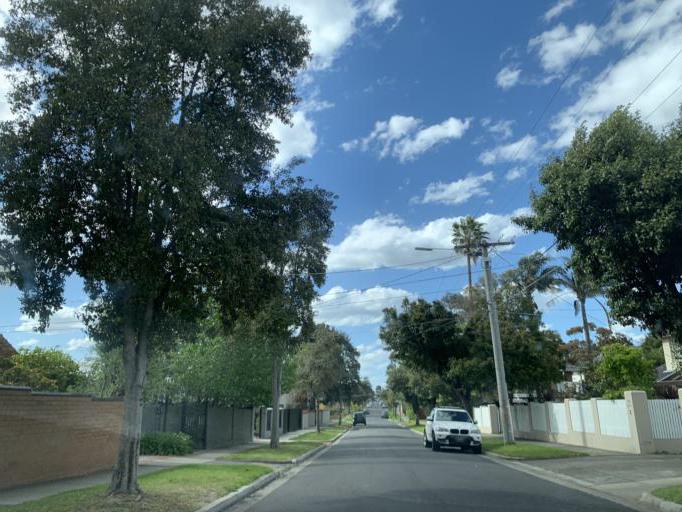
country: AU
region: Victoria
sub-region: Bayside
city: Hampton
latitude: -37.9263
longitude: 145.0131
